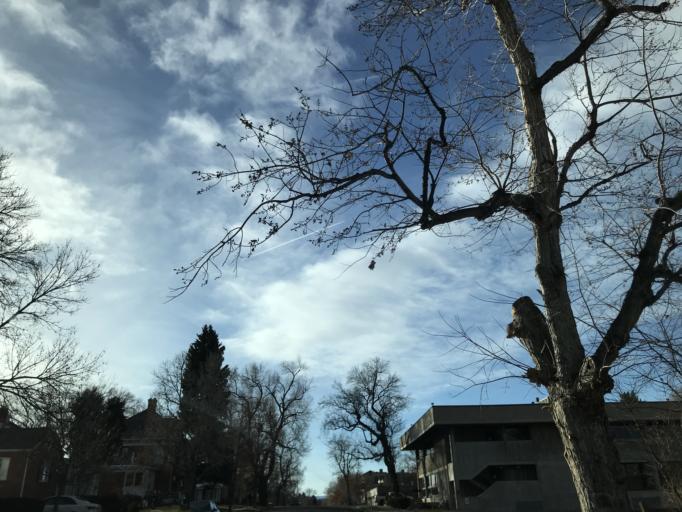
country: US
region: Colorado
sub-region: Arapahoe County
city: Littleton
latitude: 39.6142
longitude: -105.0103
